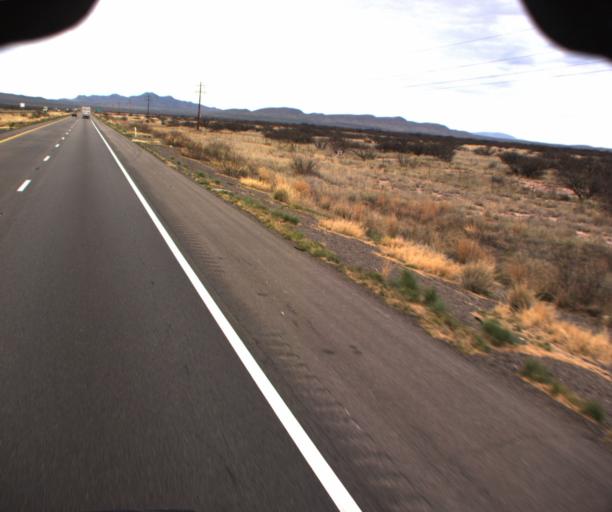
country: US
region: Arizona
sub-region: Cochise County
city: Willcox
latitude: 32.2009
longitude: -109.9087
